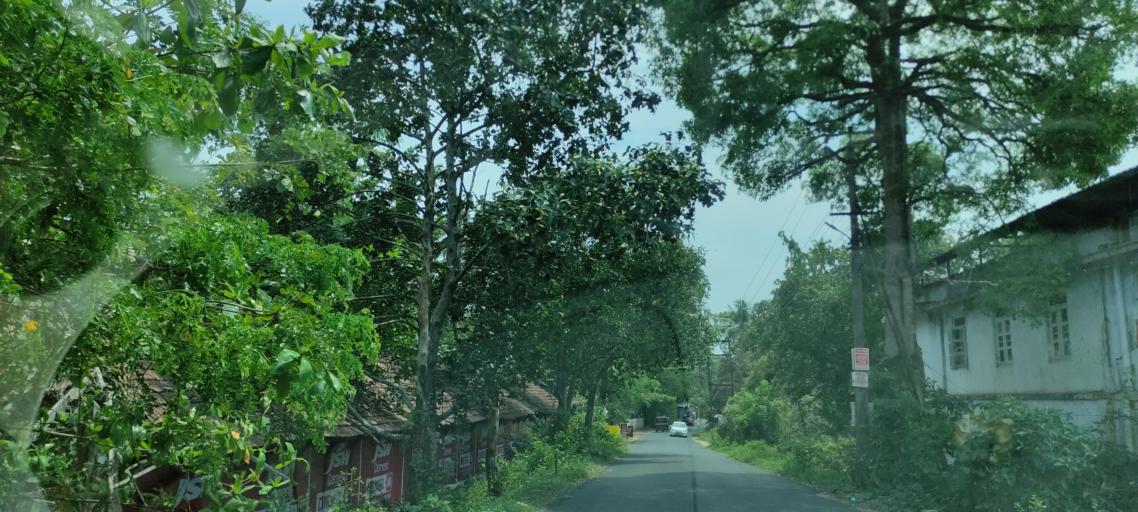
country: IN
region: Kerala
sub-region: Alappuzha
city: Vayalar
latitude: 9.6977
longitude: 76.3378
